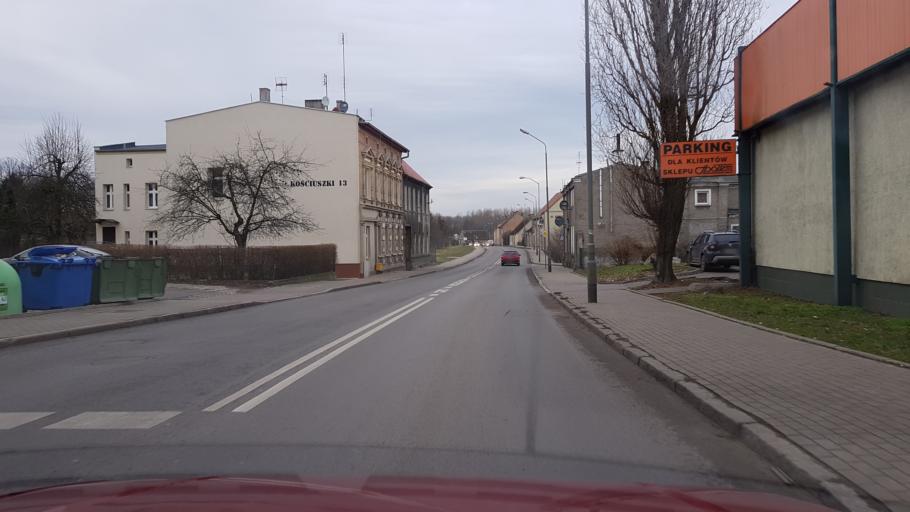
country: PL
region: West Pomeranian Voivodeship
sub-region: Powiat policki
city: Police
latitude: 53.5525
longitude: 14.5719
